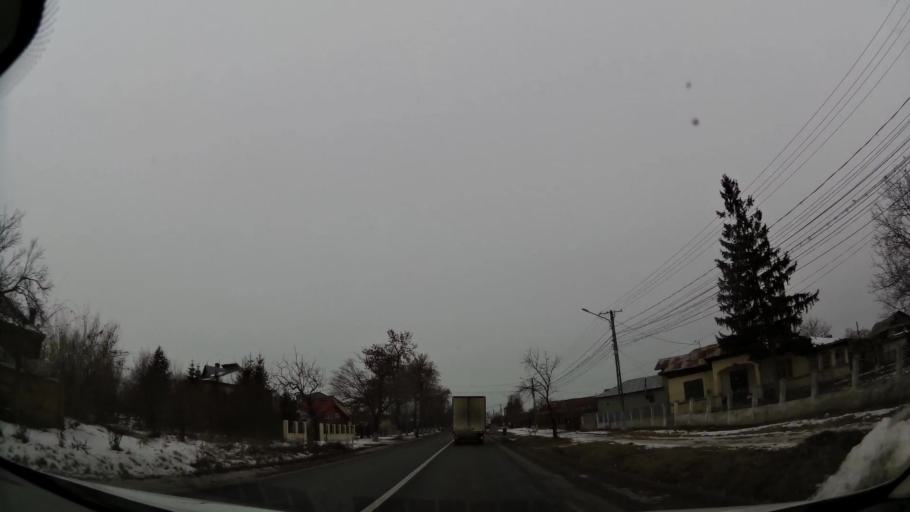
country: RO
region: Dambovita
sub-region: Comuna Tartasesti
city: Baldana
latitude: 44.6028
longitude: 25.7760
